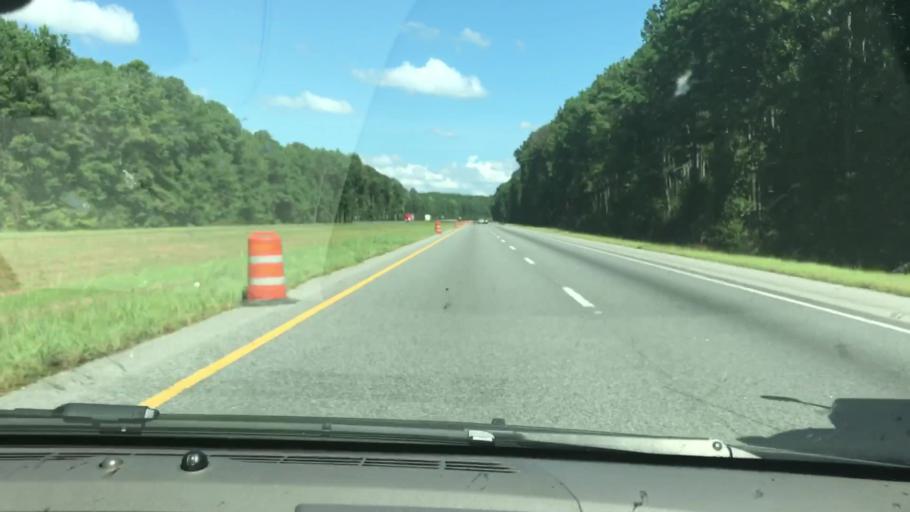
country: US
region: Georgia
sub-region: Harris County
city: Hamilton
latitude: 32.7106
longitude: -85.0132
